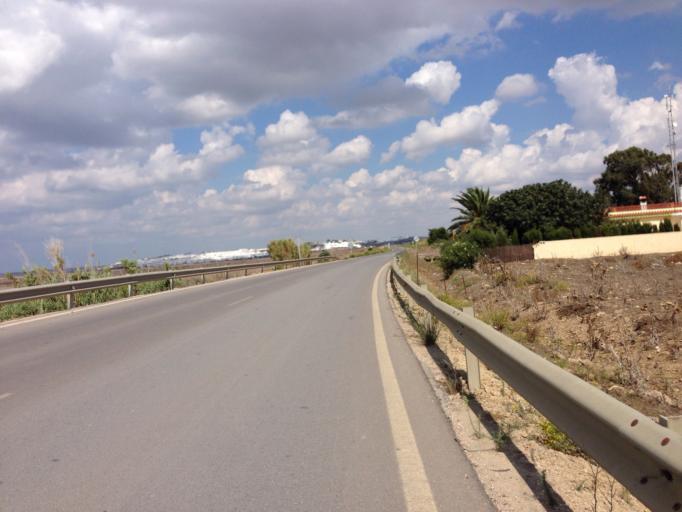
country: ES
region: Andalusia
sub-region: Provincia de Cadiz
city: Conil de la Frontera
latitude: 36.2519
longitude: -6.0689
